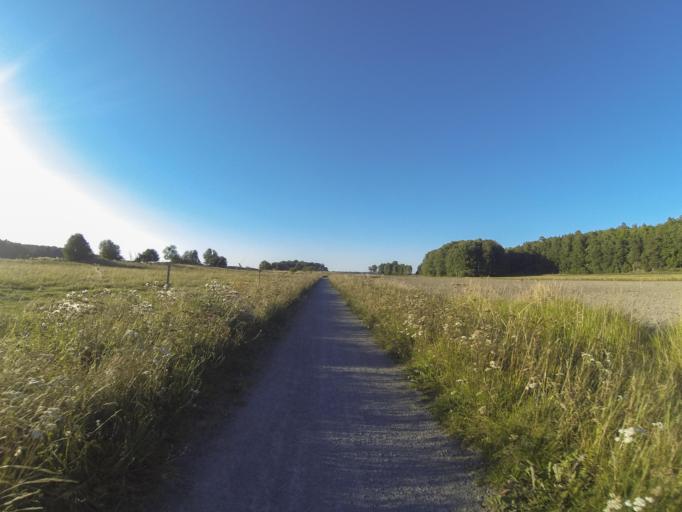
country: SE
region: Vaestmanland
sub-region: Vasteras
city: Vasteras
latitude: 59.5680
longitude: 16.6493
